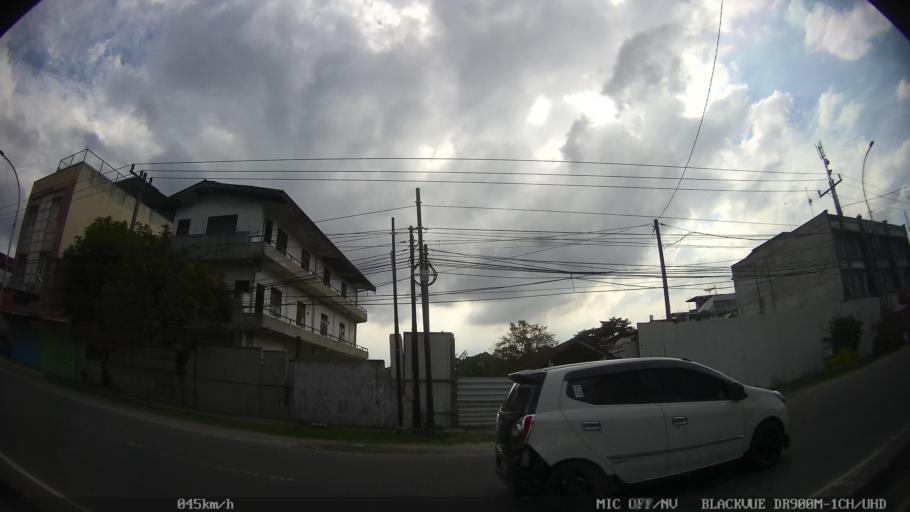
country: ID
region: North Sumatra
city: Medan
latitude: 3.6156
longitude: 98.6720
